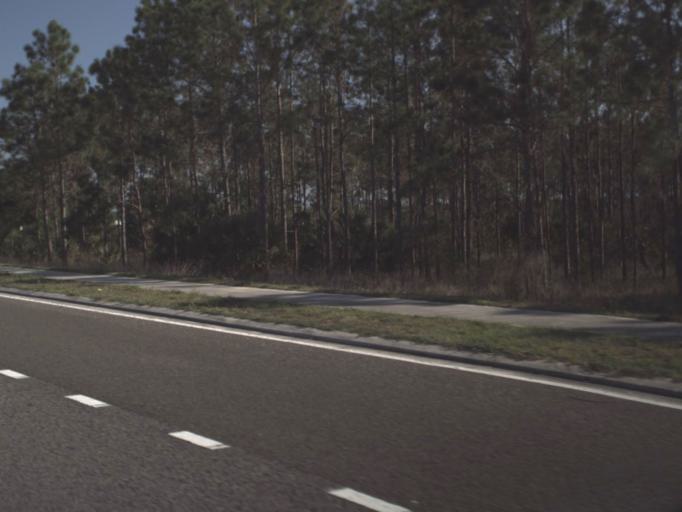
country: US
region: Florida
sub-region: Lake County
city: Four Corners
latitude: 28.3781
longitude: -81.6866
